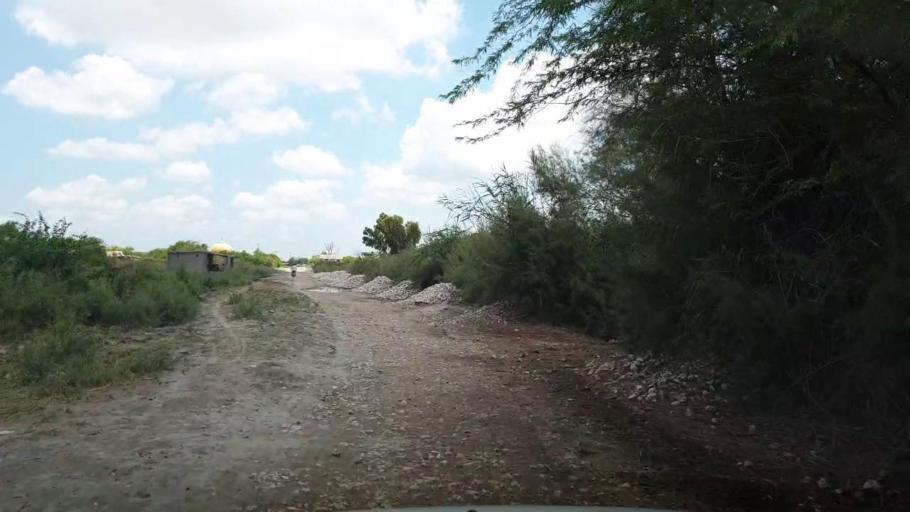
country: PK
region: Sindh
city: Jhol
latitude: 25.8975
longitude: 69.0081
